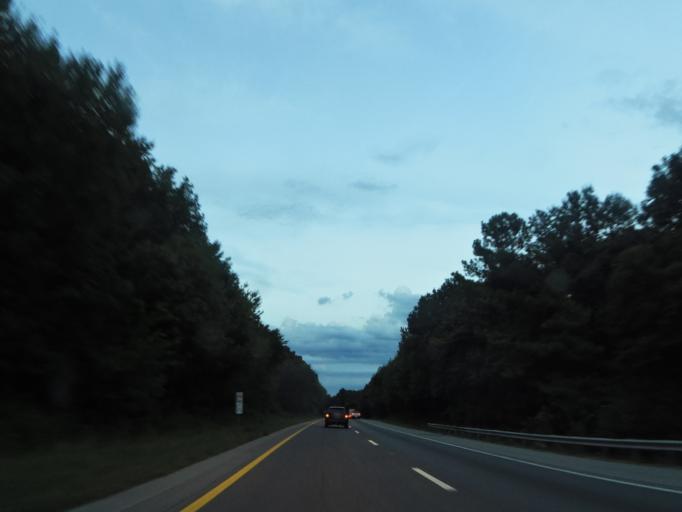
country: US
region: Tennessee
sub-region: Roane County
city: Rockwood
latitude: 35.8957
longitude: -84.6589
